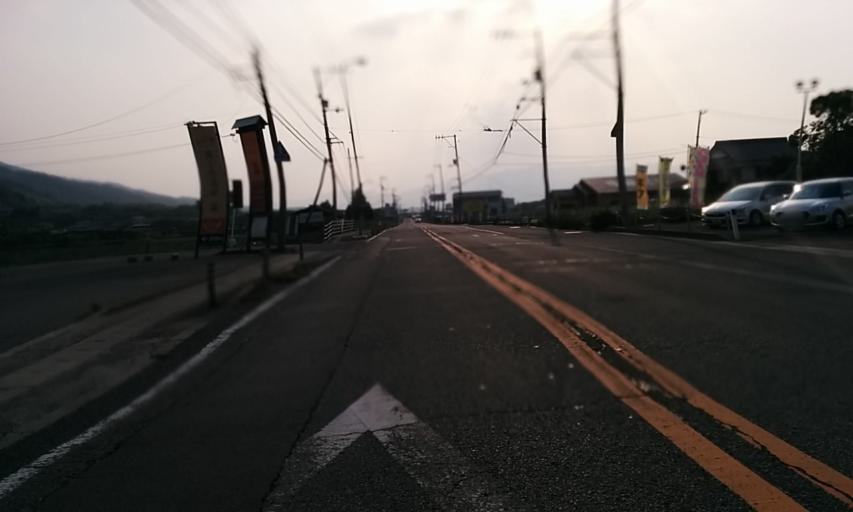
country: JP
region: Ehime
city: Saijo
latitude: 33.8951
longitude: 133.1632
